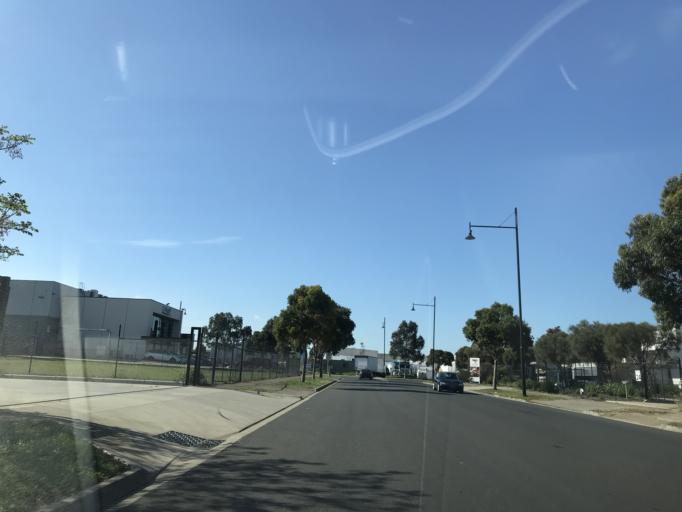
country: AU
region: Victoria
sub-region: Wyndham
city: Truganina
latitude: -37.8097
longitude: 144.7556
